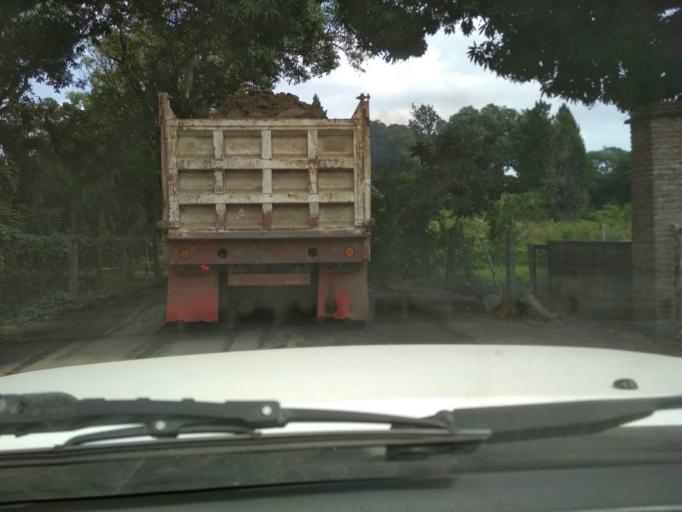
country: MX
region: Veracruz
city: El Tejar
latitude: 19.0826
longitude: -96.1717
